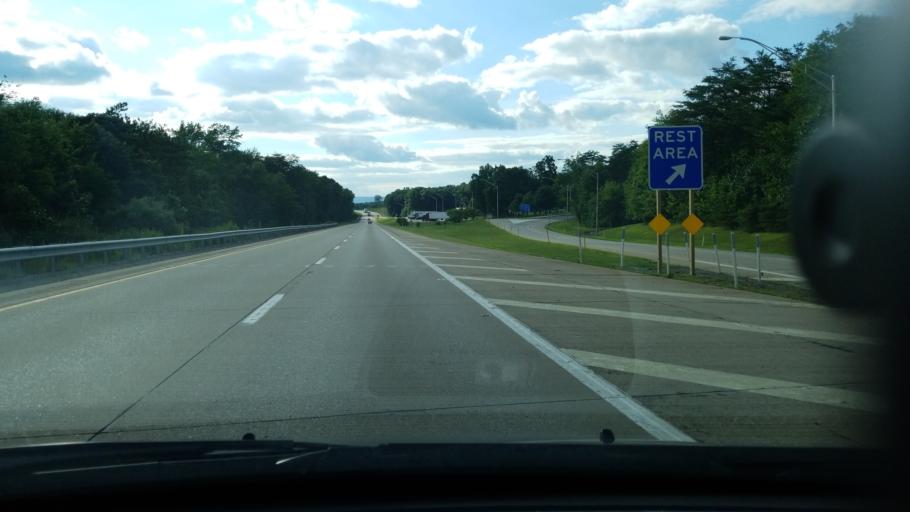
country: US
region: Pennsylvania
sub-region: Northumberland County
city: Riverside
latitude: 40.9881
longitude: -76.7221
